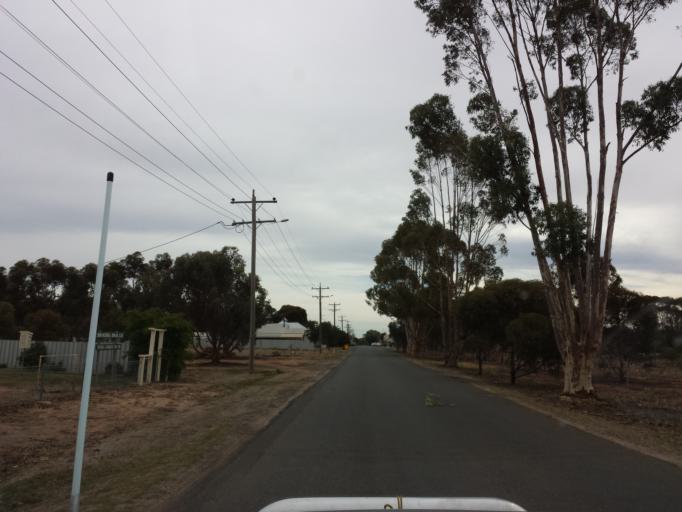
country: AU
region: Victoria
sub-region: Horsham
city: Horsham
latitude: -36.0761
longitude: 142.4189
